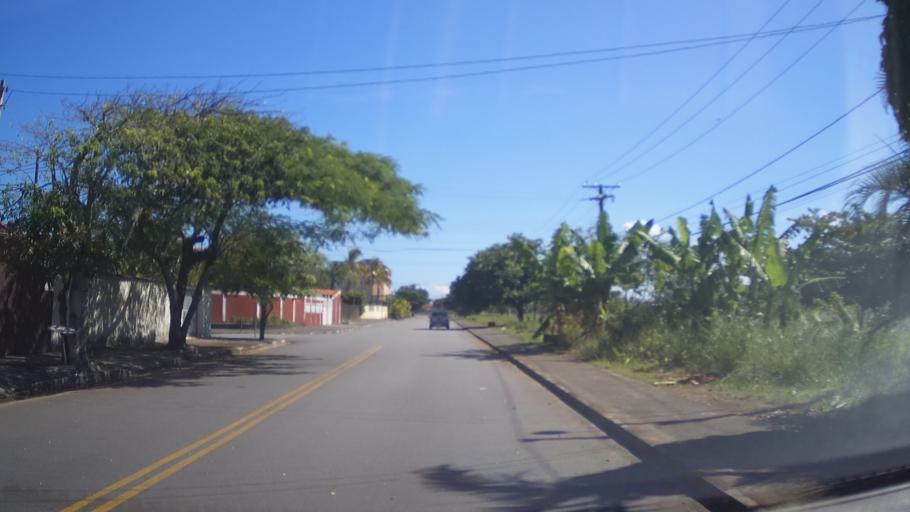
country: BR
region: Sao Paulo
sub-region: Mongagua
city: Mongagua
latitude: -24.1220
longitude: -46.6746
